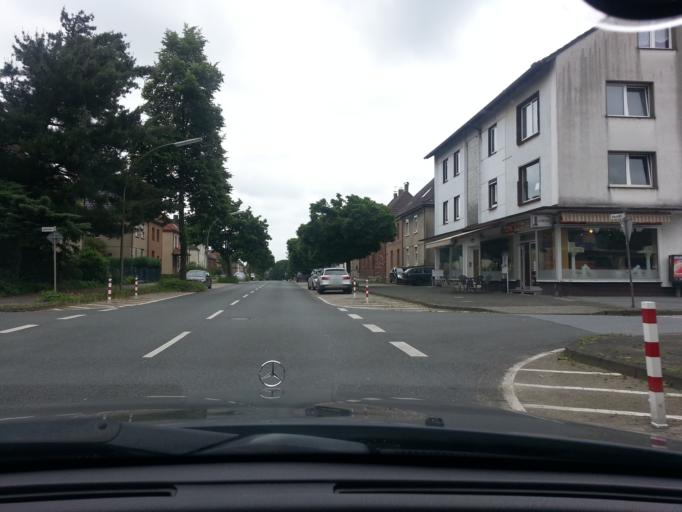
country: DE
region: North Rhine-Westphalia
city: Oer-Erkenschwick
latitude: 51.6486
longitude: 7.2492
